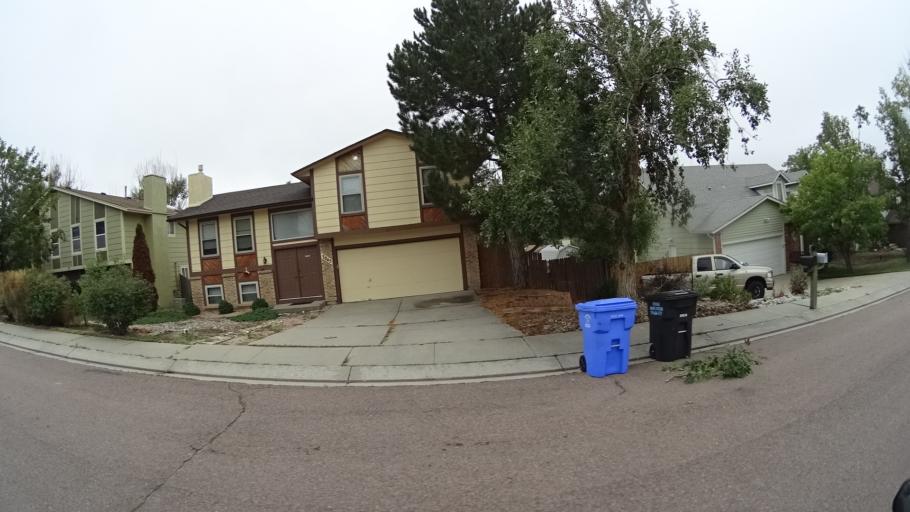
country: US
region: Colorado
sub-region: El Paso County
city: Cimarron Hills
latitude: 38.9334
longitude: -104.7644
